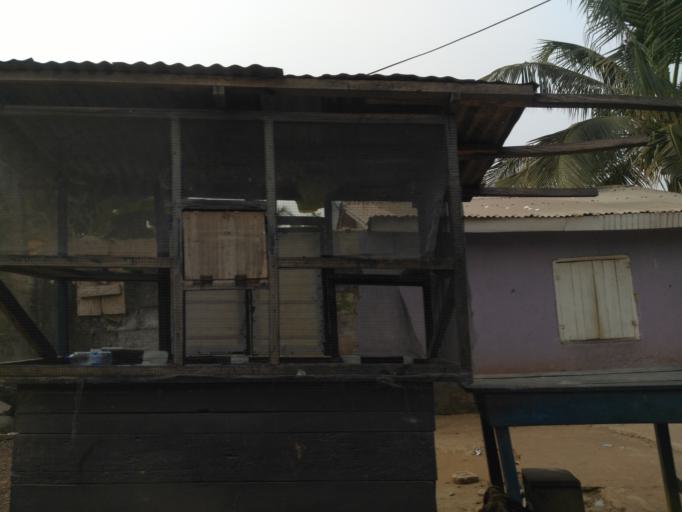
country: GH
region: Ashanti
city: Kumasi
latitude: 6.6513
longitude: -1.6191
